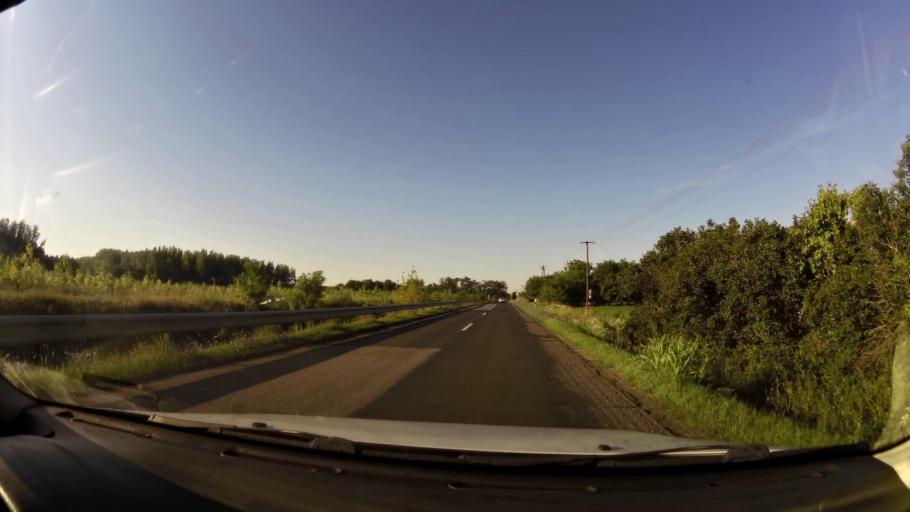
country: HU
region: Pest
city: Tapioszolos
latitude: 47.2761
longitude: 19.8654
